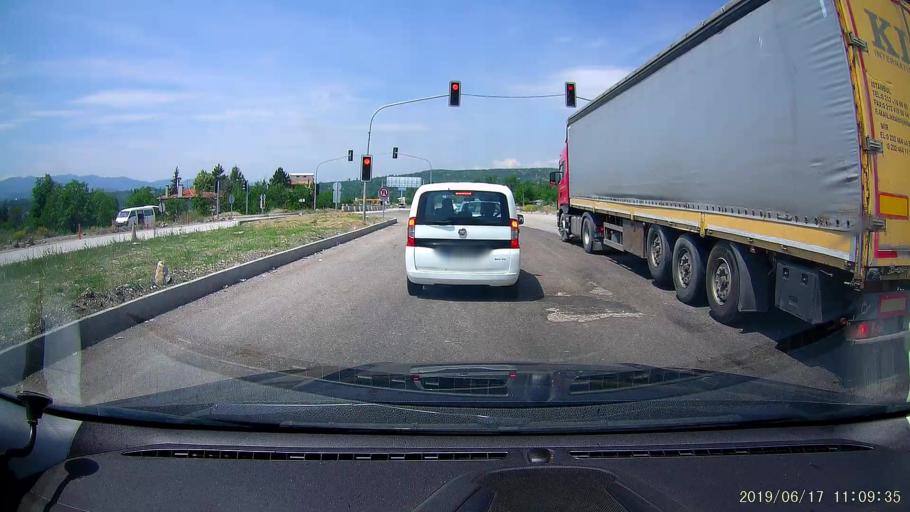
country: TR
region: Kastamonu
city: Tosya
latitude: 41.0022
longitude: 34.0317
